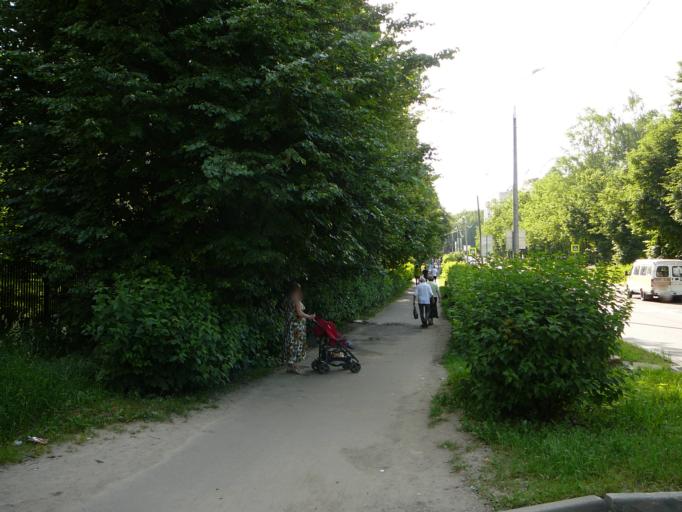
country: RU
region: Moskovskaya
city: Krasnogorsk
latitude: 55.8170
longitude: 37.3142
